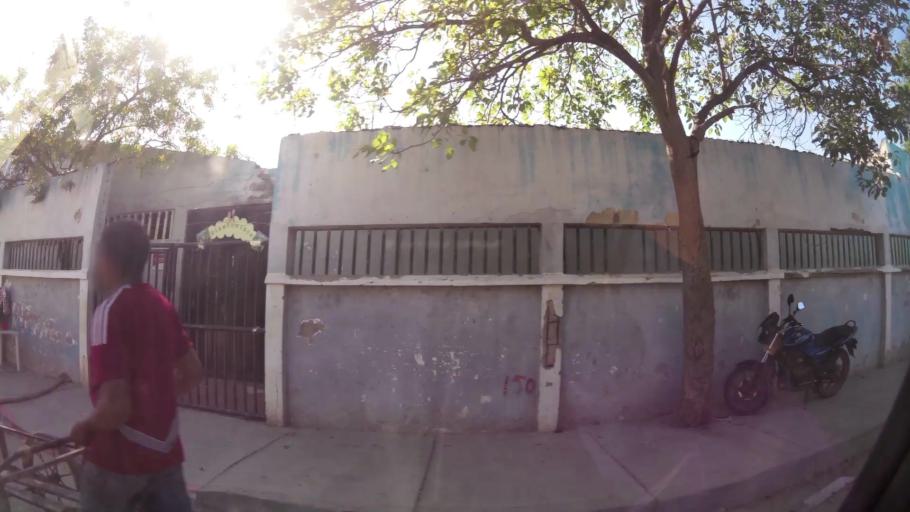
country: CO
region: Bolivar
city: Cartagena
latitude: 10.4163
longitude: -75.5159
